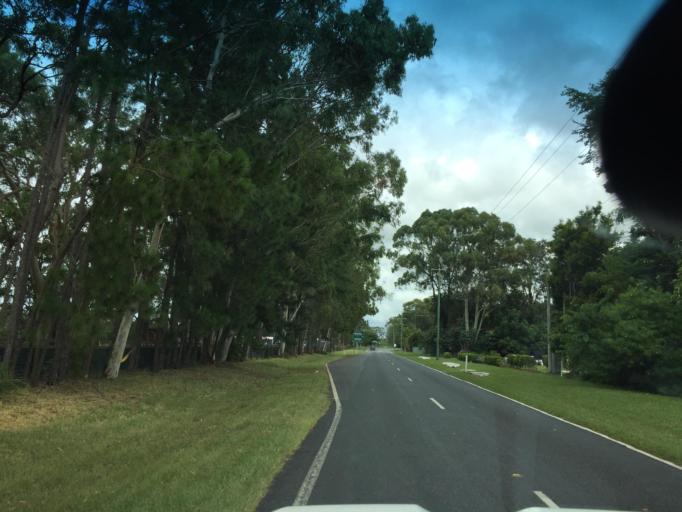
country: AU
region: Queensland
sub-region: Moreton Bay
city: Caboolture
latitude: -27.0572
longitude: 152.9106
